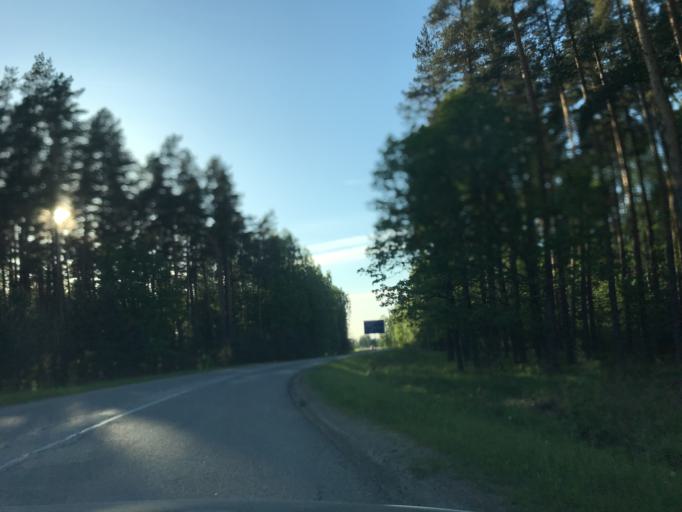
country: LV
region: Jelgava
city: Jelgava
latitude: 56.6261
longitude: 23.7599
